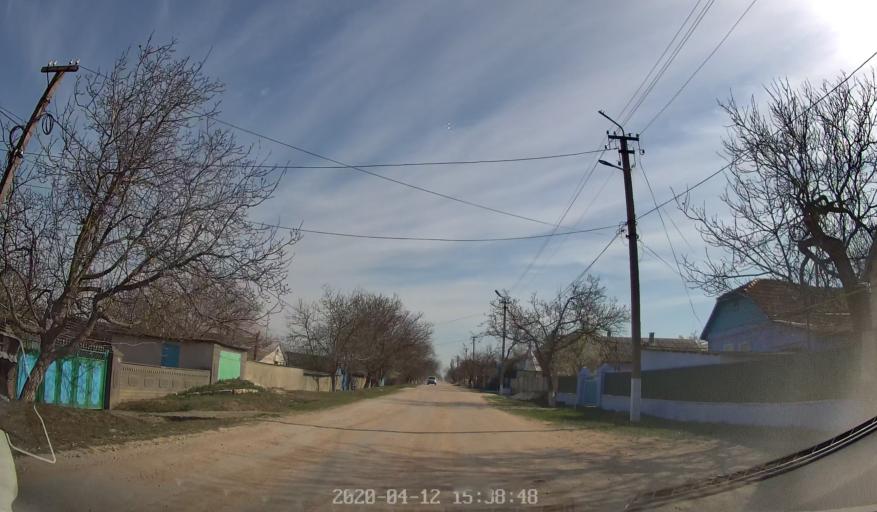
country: MD
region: Telenesti
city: Cocieri
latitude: 47.3174
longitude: 29.0699
